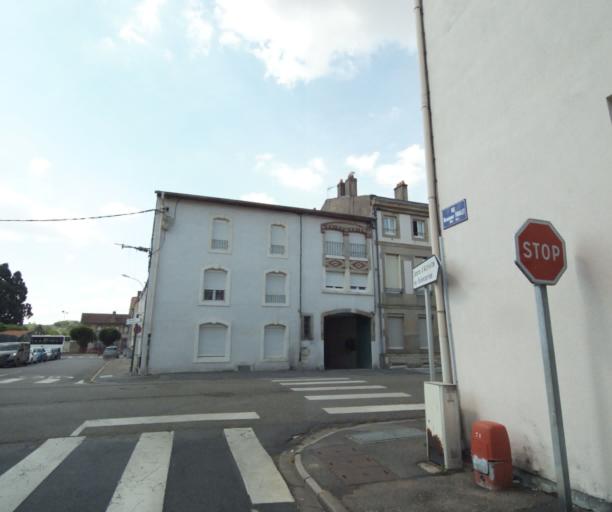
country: FR
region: Lorraine
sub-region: Departement de Meurthe-et-Moselle
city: Luneville
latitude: 48.5866
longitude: 6.4871
